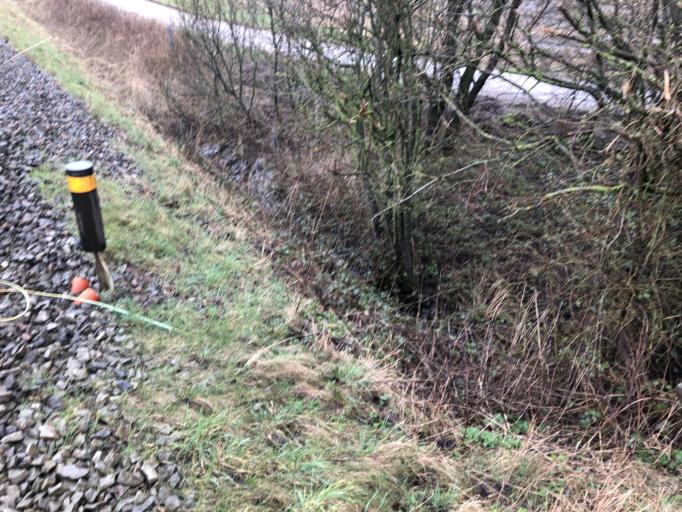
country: DK
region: South Denmark
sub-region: Aabenraa Kommune
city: Krusa
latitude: 54.9141
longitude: 9.4808
